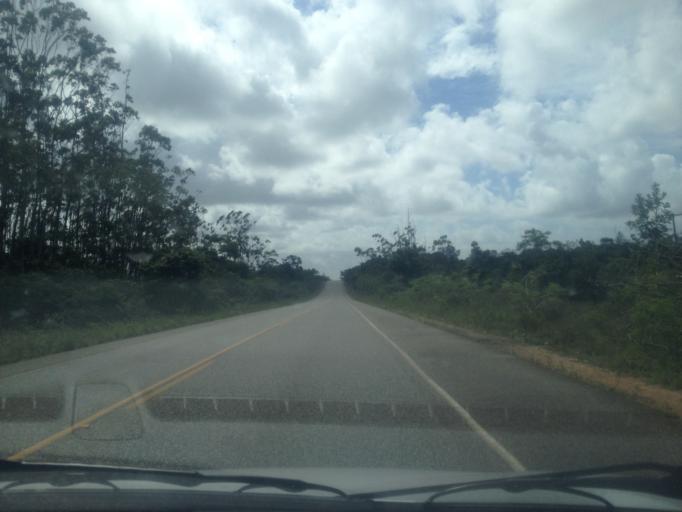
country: BR
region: Bahia
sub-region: Entre Rios
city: Entre Rios
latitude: -12.2848
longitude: -37.8873
